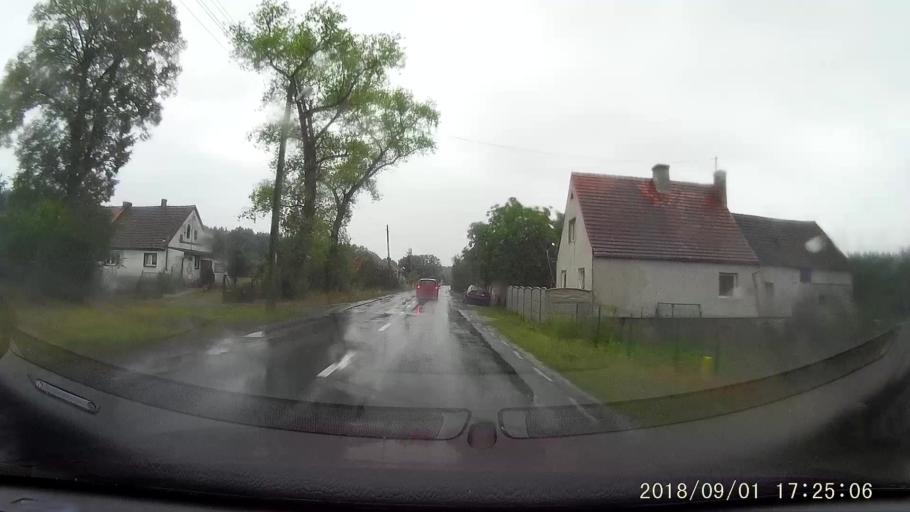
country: PL
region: Lubusz
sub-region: Powiat zaganski
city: Zagan
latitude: 51.6887
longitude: 15.3066
